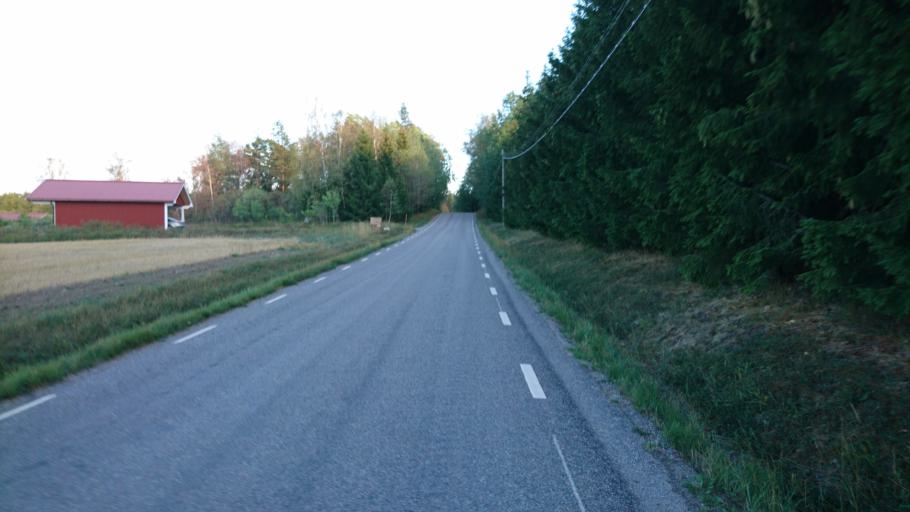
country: SE
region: Soedermanland
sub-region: Strangnas Kommun
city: Stallarholmen
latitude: 59.3967
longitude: 17.2659
